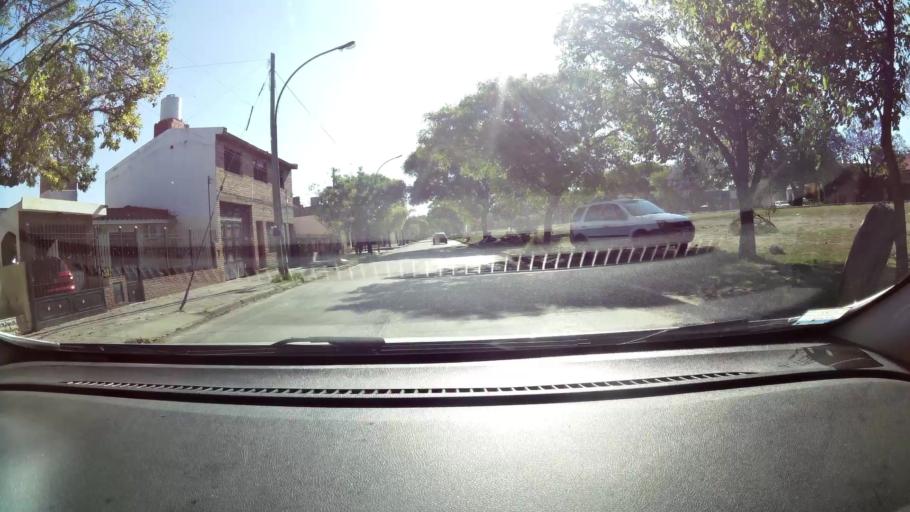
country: AR
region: Cordoba
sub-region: Departamento de Capital
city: Cordoba
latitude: -31.3921
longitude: -64.1458
